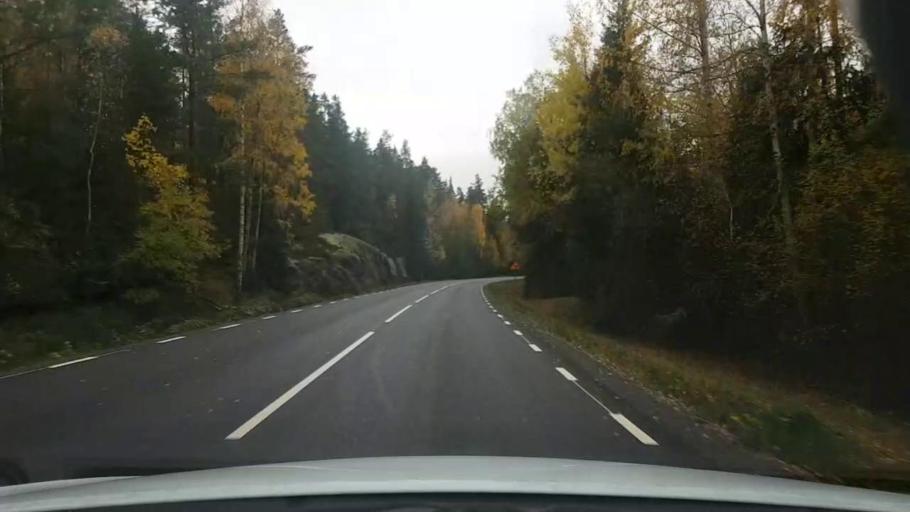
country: SE
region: OErebro
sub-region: Laxa Kommun
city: Laxa
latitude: 58.8160
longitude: 14.5506
